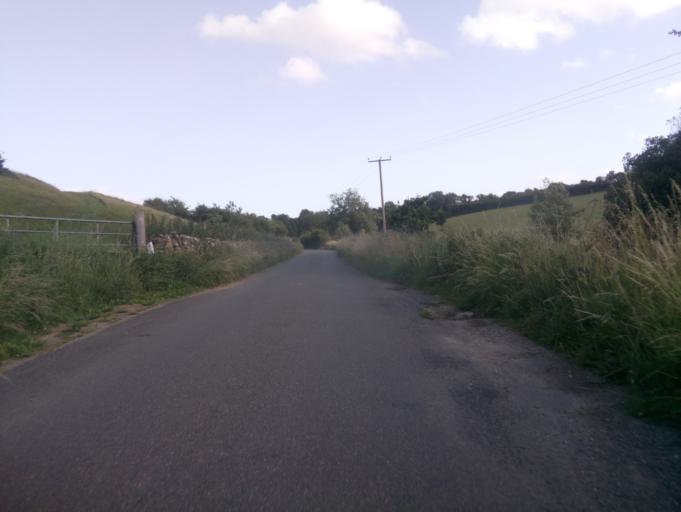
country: GB
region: England
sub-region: Gloucestershire
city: Westfield
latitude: 51.9085
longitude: -1.8233
